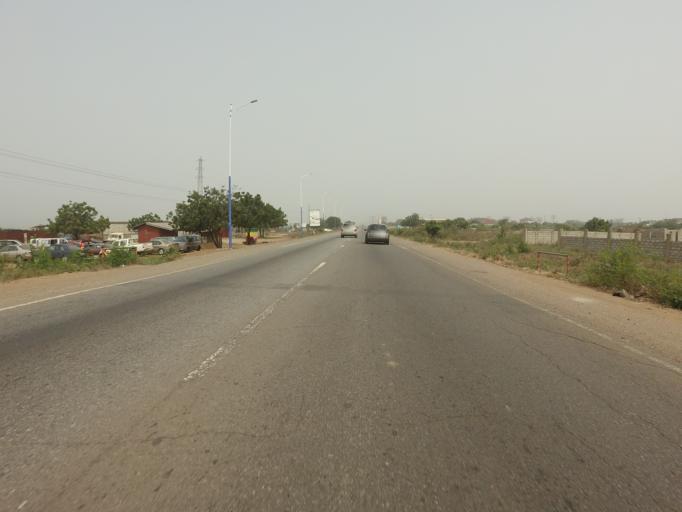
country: GH
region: Greater Accra
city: Tema
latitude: 5.7696
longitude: 0.0682
